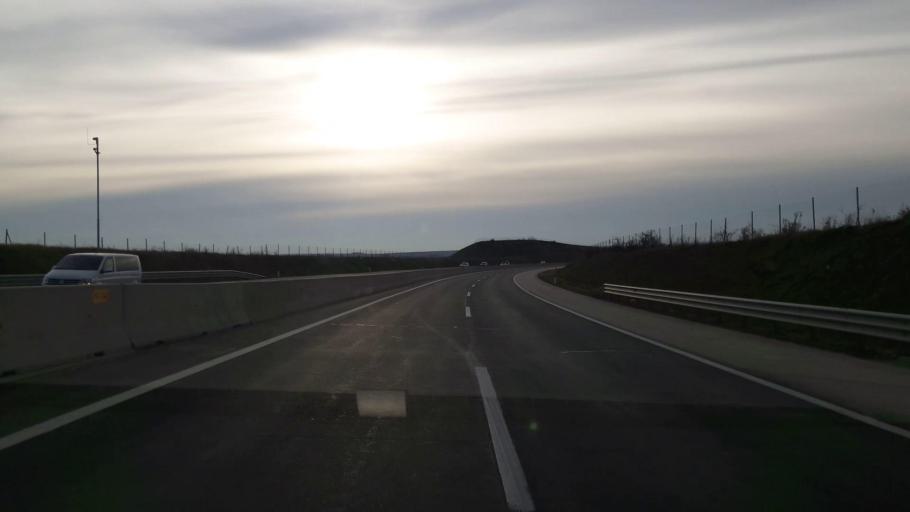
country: AT
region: Lower Austria
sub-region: Politischer Bezirk Mistelbach
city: Gaweinstal
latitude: 48.4946
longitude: 16.5972
